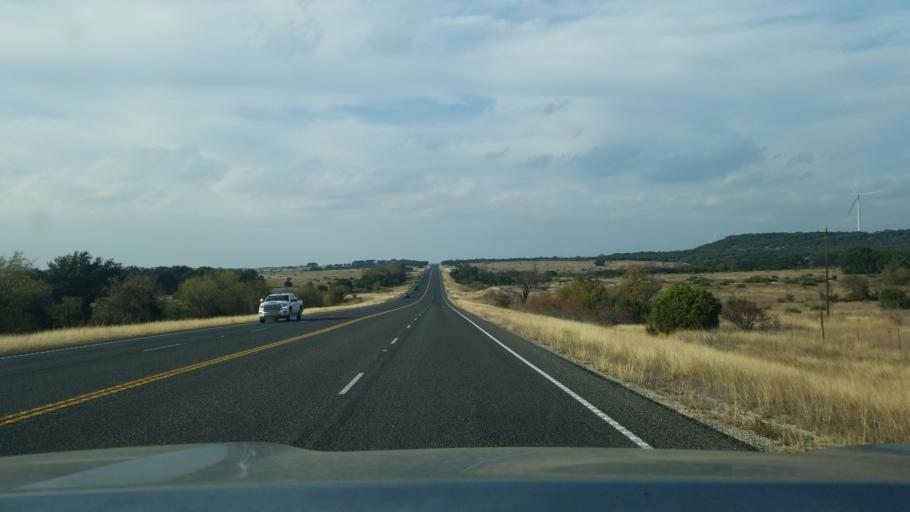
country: US
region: Texas
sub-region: Mills County
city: Goldthwaite
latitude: 31.3233
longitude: -98.4903
